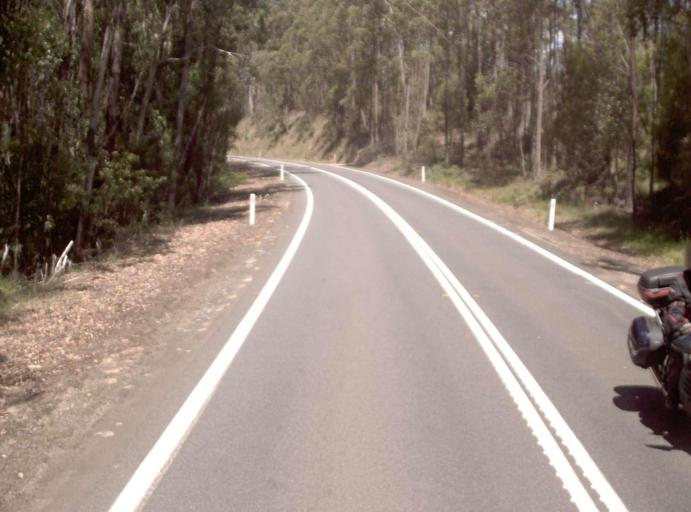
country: AU
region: New South Wales
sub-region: Bombala
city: Bombala
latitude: -37.5849
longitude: 148.9487
